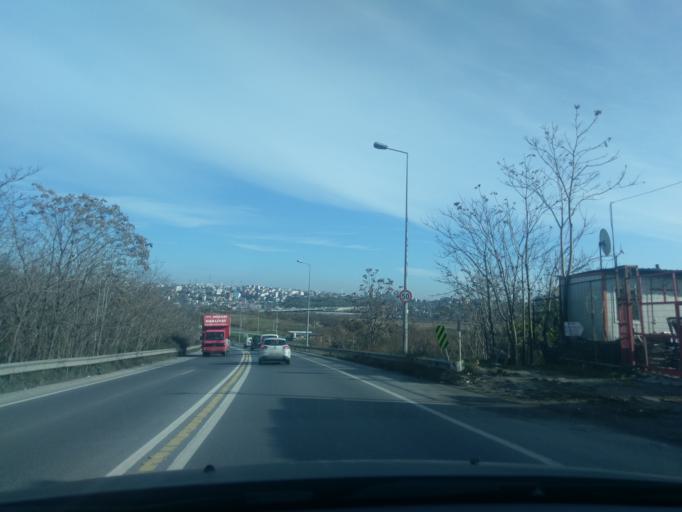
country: TR
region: Istanbul
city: Esenyurt
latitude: 41.0558
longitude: 28.7299
